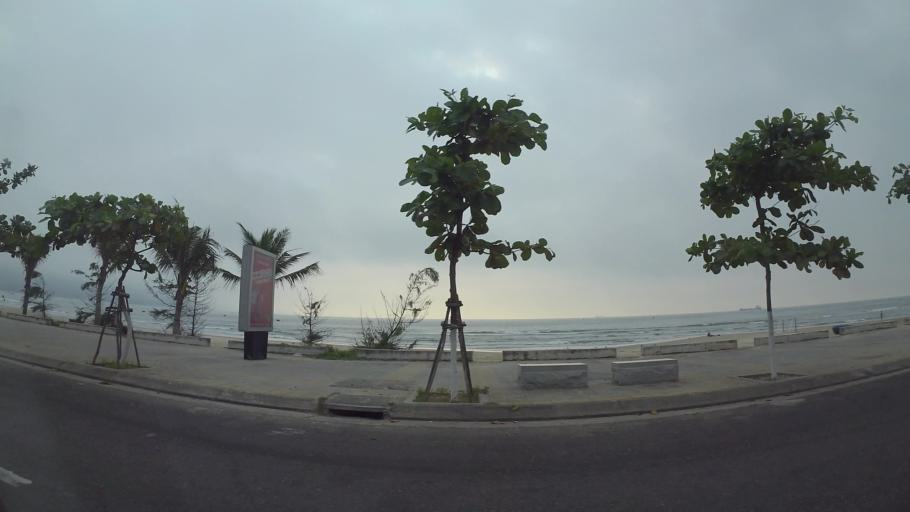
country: VN
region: Da Nang
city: Son Tra
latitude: 16.0841
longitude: 108.2481
